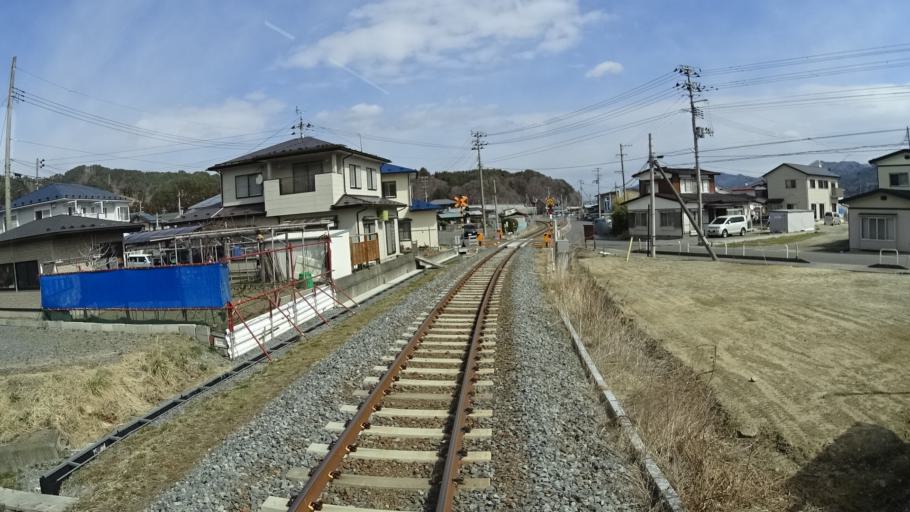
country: JP
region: Iwate
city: Miyako
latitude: 39.5783
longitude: 141.9356
